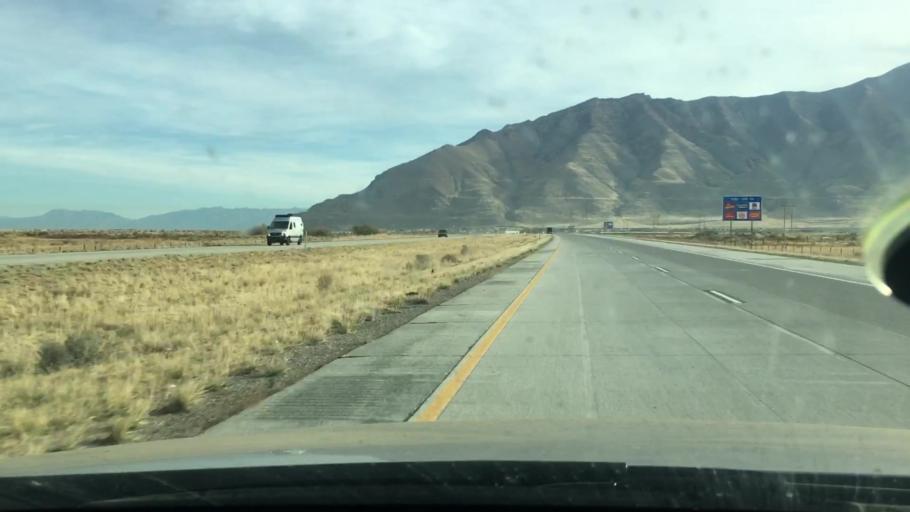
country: US
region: Utah
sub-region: Tooele County
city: Stansbury park
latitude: 40.6709
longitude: -112.2957
